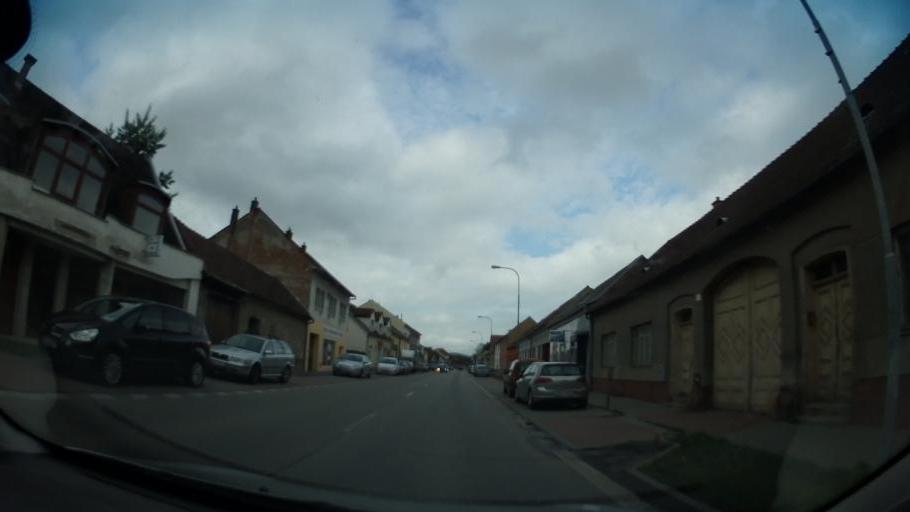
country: CZ
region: South Moravian
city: Kurim
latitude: 49.2981
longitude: 16.5370
